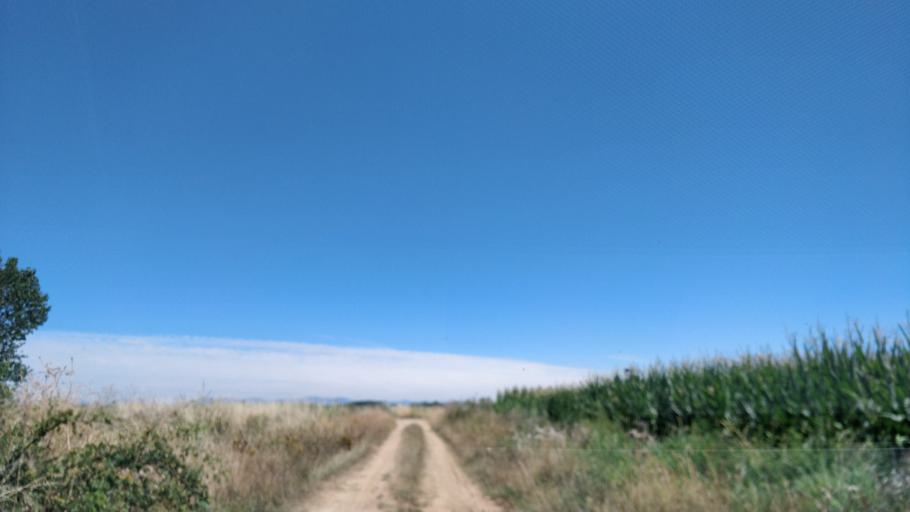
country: ES
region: Castille and Leon
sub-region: Provincia de Leon
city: Bustillo del Paramo
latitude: 42.4645
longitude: -5.8151
